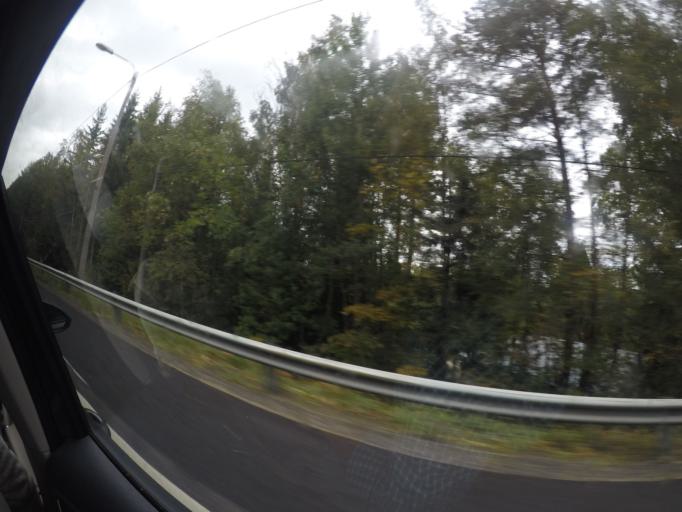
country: FI
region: Pirkanmaa
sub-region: Tampere
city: Kangasala
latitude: 61.4449
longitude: 24.1124
